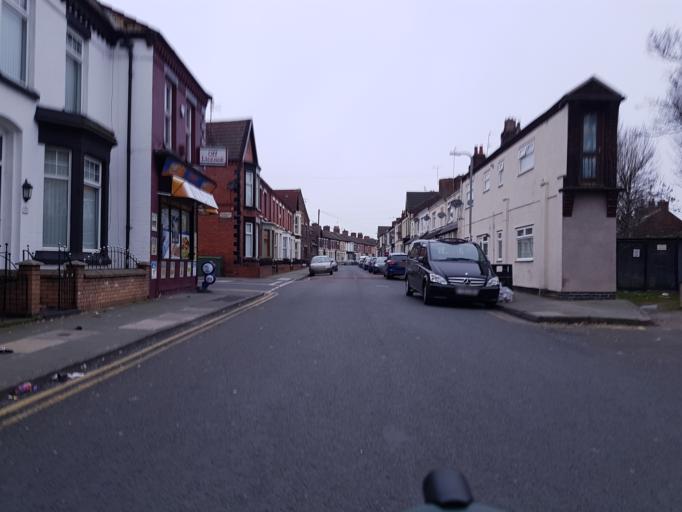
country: GB
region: England
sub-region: Liverpool
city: Liverpool
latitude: 53.4441
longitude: -2.9641
